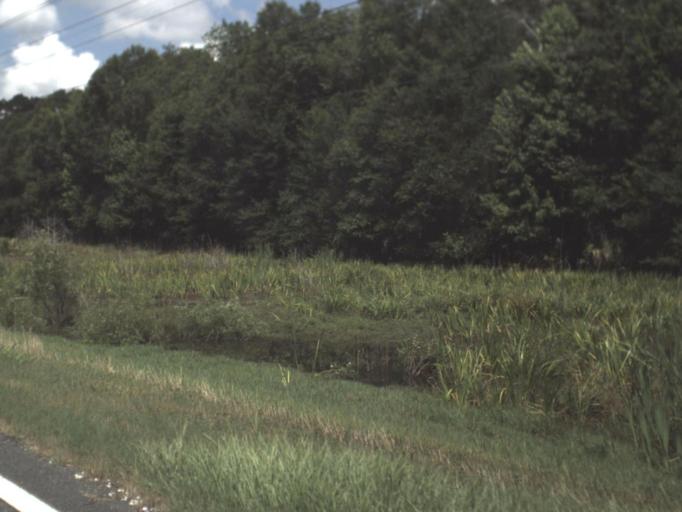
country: US
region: Florida
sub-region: Levy County
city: Chiefland
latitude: 29.2670
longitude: -82.8763
